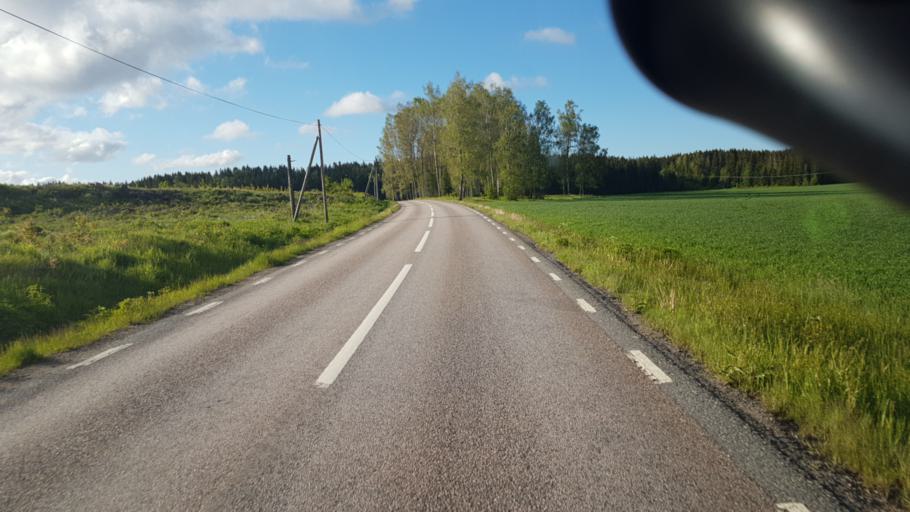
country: SE
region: Vaermland
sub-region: Arvika Kommun
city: Arvika
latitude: 59.5919
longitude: 12.5383
